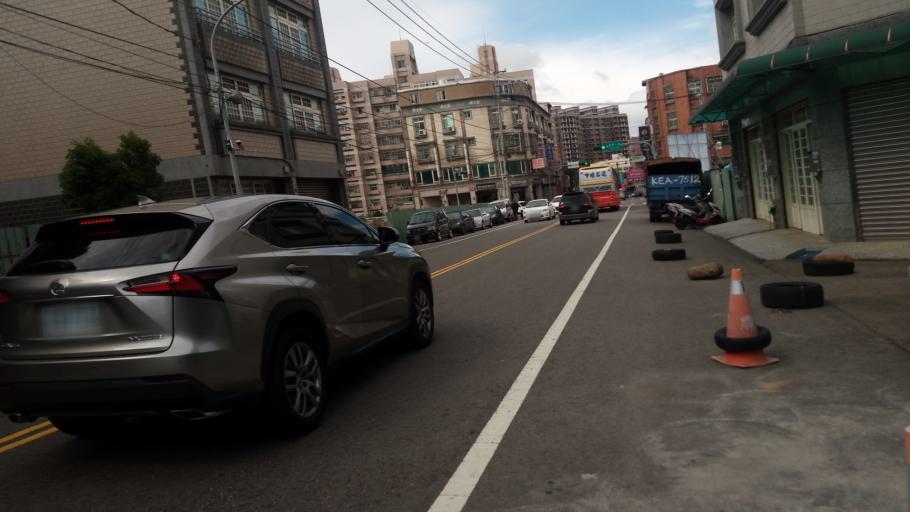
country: TW
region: Taiwan
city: Daxi
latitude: 24.9379
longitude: 121.2465
